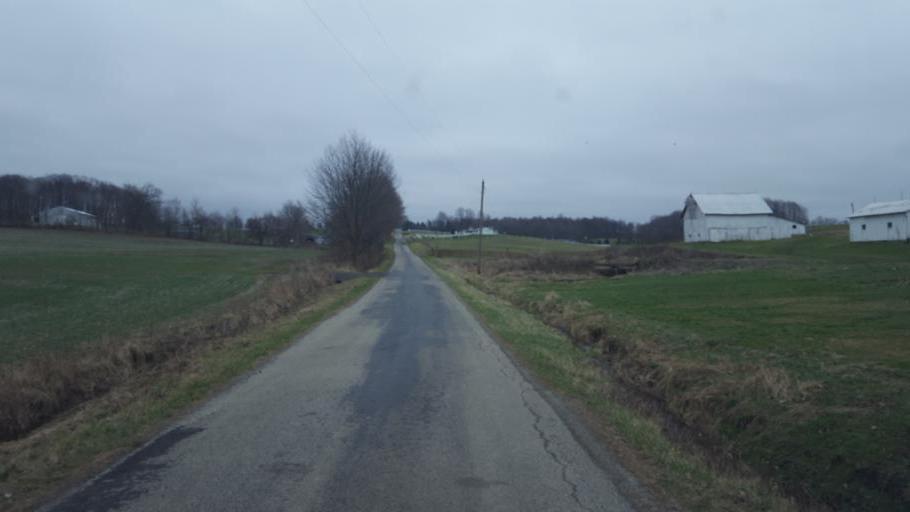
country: US
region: Ohio
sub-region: Knox County
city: Mount Vernon
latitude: 40.4489
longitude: -82.4823
